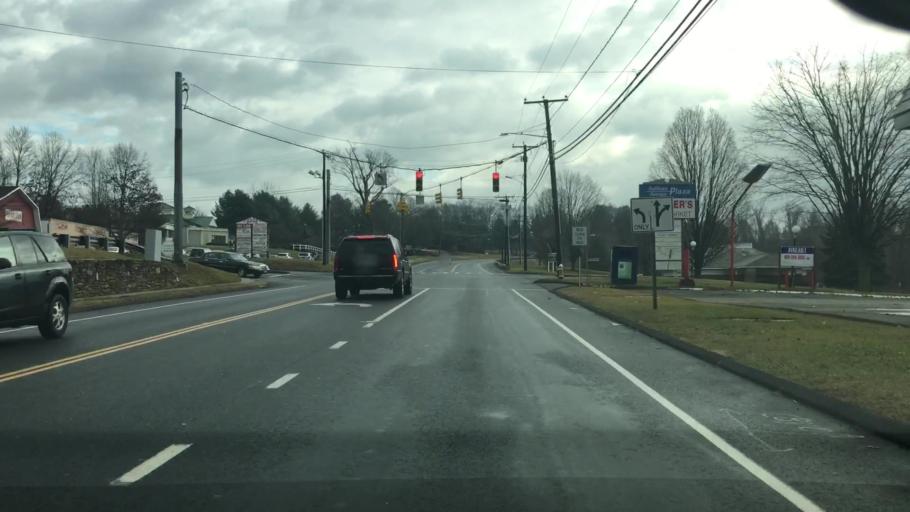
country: US
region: Connecticut
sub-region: Hartford County
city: South Windsor
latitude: 41.8464
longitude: -72.5634
